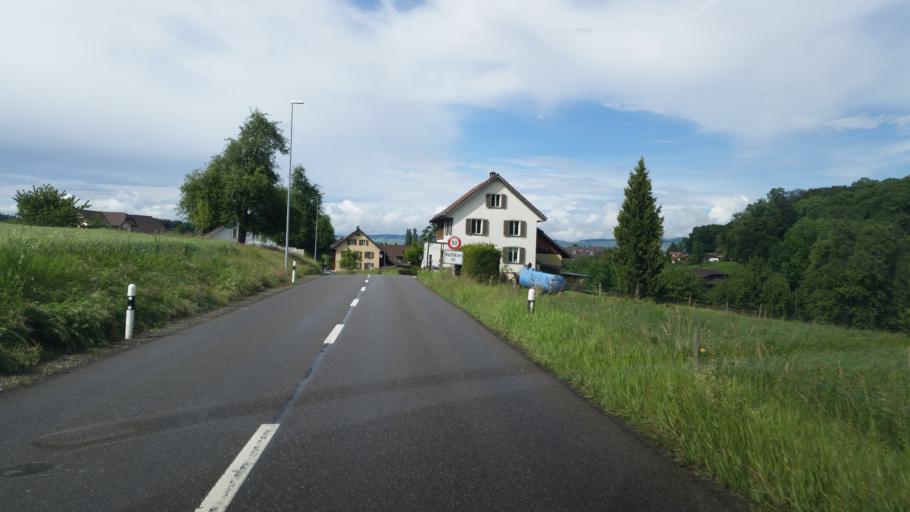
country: CH
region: Aargau
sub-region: Bezirk Bremgarten
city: Sarmenstorf
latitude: 47.3233
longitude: 8.2676
